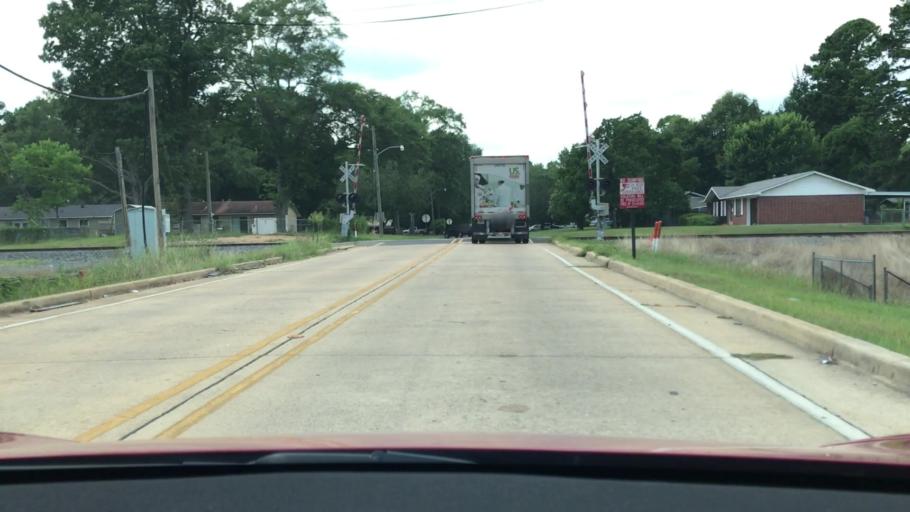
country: US
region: Louisiana
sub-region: De Soto Parish
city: Stonewall
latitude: 32.3947
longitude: -93.7994
